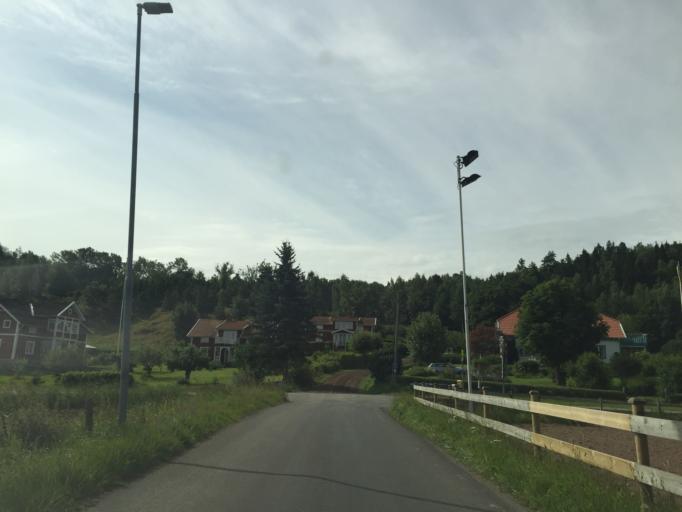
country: SE
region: Joenkoeping
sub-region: Jonkopings Kommun
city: Kaxholmen
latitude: 57.8565
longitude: 14.2815
